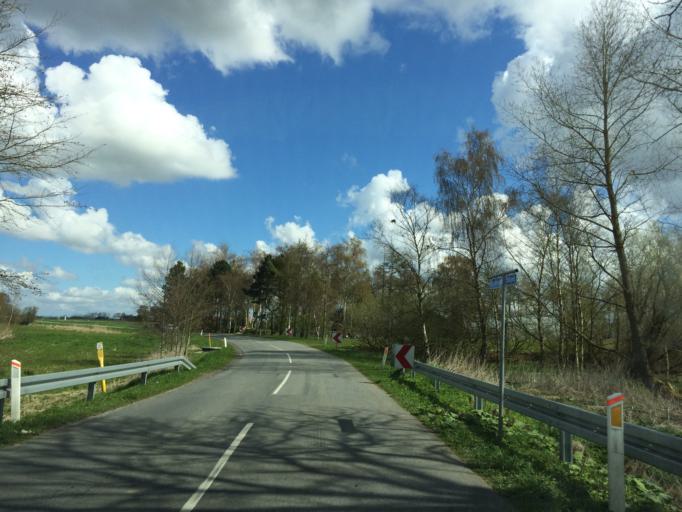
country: DK
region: South Denmark
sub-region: Odense Kommune
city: Bellinge
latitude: 55.2602
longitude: 10.2889
